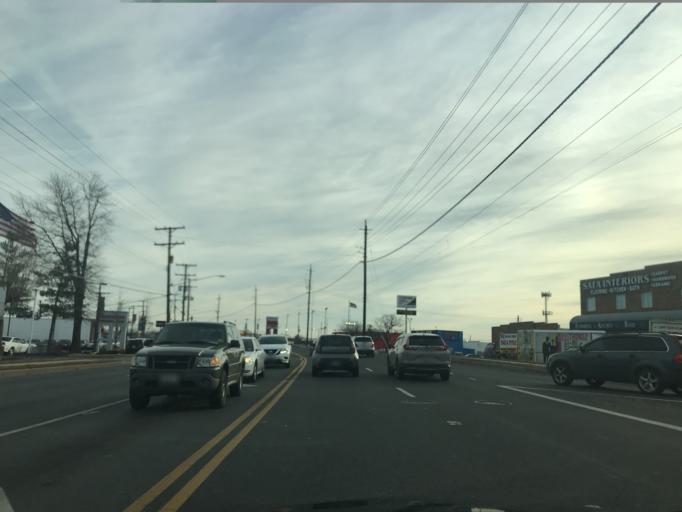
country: US
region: Maryland
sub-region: Prince George's County
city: Marlow Heights
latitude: 38.8234
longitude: -76.9500
